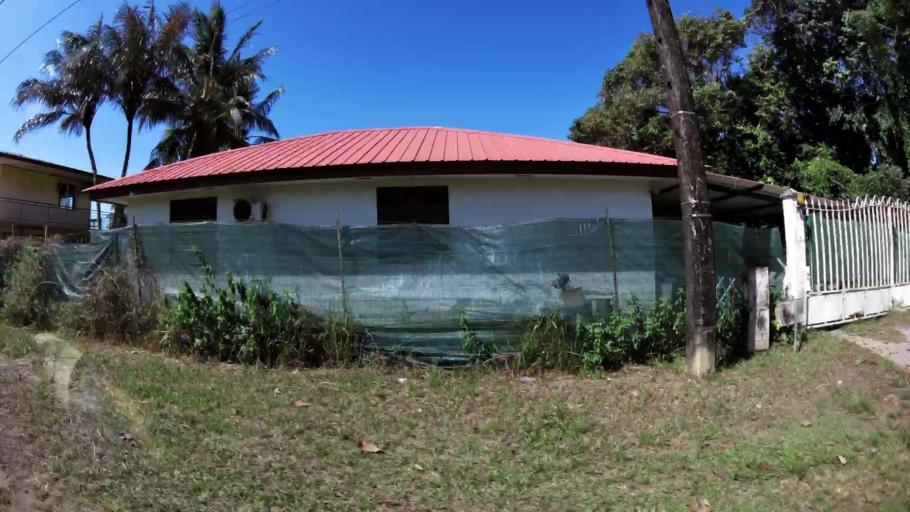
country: GF
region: Guyane
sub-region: Guyane
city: Remire-Montjoly
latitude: 4.9168
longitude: -52.2667
